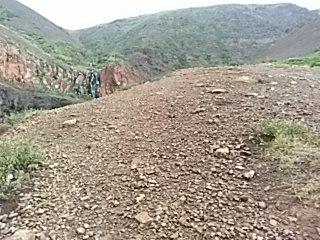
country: RU
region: Krasnoyarskiy
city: Talnakh
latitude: 69.4794
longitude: 88.5314
